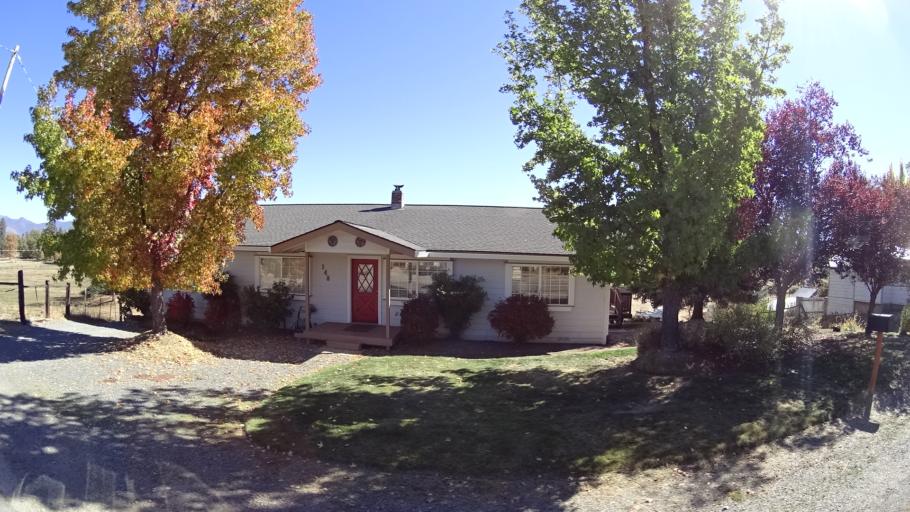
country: US
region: California
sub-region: Siskiyou County
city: Yreka
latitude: 41.4593
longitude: -122.8900
